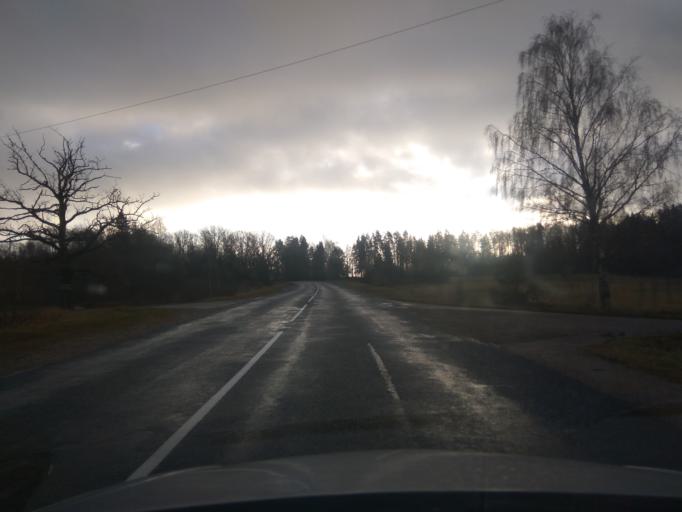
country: LV
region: Kuldigas Rajons
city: Kuldiga
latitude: 56.8998
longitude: 22.0785
